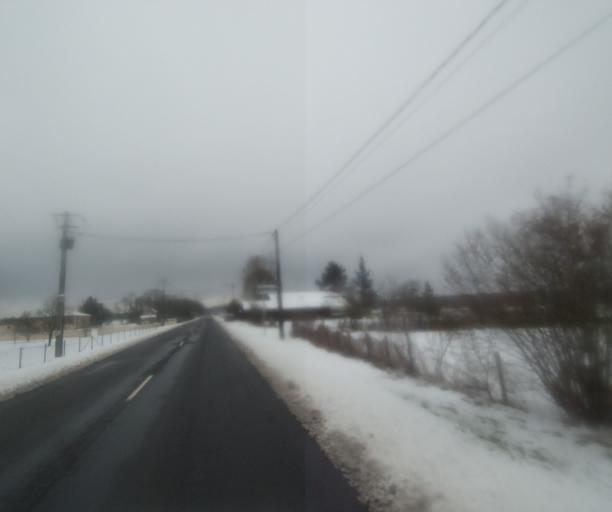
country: FR
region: Champagne-Ardenne
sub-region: Departement de la Haute-Marne
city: Laneuville-a-Remy
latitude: 48.4933
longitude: 4.8645
